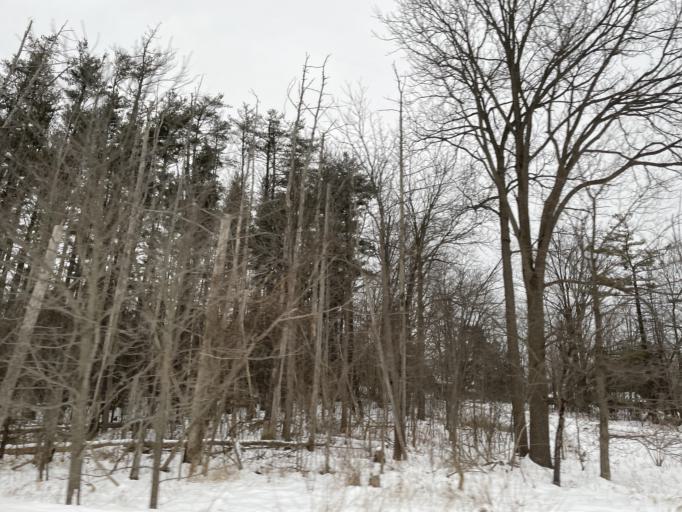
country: CA
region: Ontario
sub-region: Wellington County
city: Guelph
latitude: 43.5117
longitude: -80.3510
